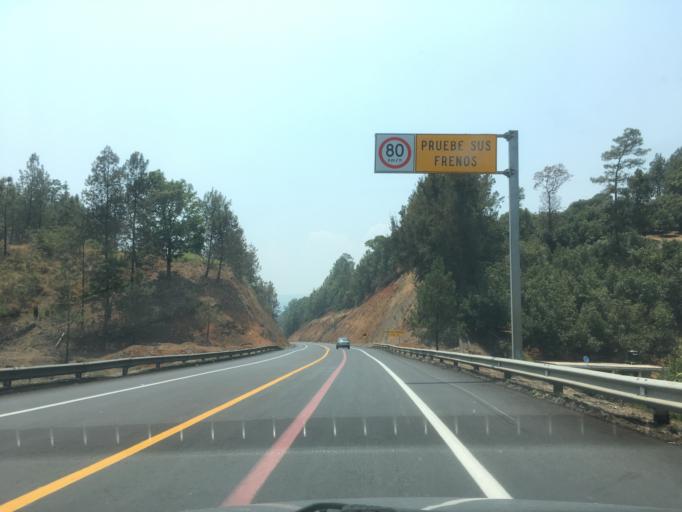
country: MX
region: Michoacan
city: Tingambato
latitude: 19.4452
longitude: -101.8494
